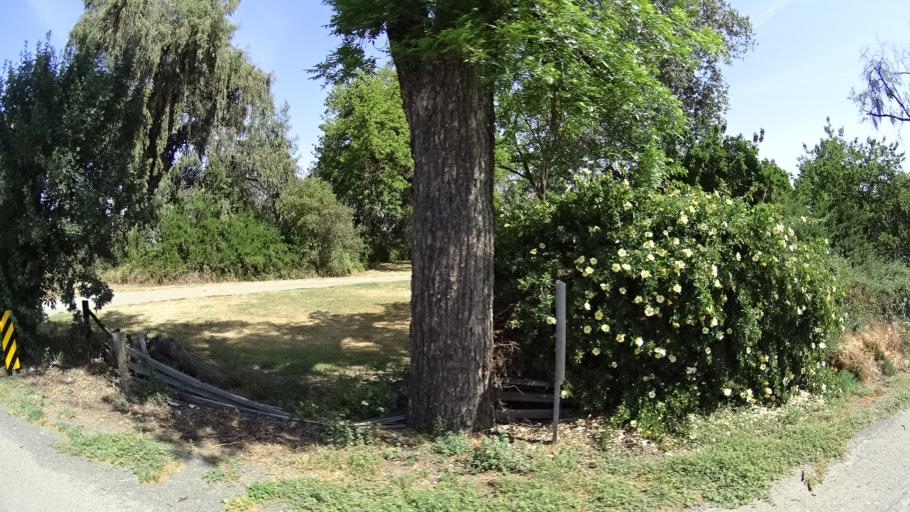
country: US
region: California
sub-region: Kings County
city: Armona
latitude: 36.3426
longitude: -119.6980
